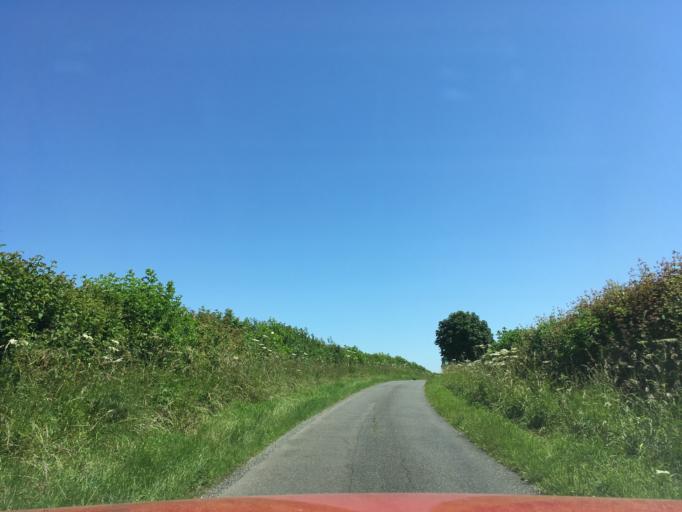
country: GB
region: England
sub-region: Northamptonshire
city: Brackley
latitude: 52.0096
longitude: -1.0818
